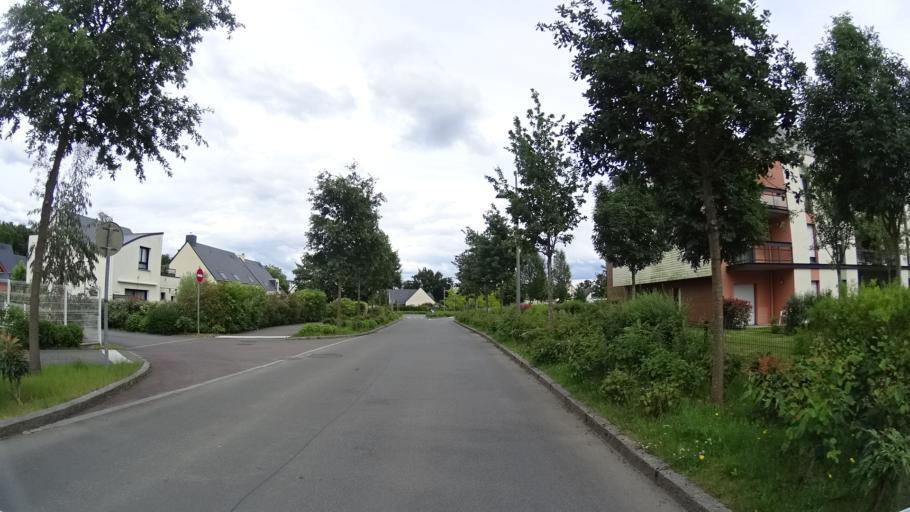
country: FR
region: Brittany
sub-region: Departement d'Ille-et-Vilaine
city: Laille
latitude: 47.9817
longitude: -1.7240
